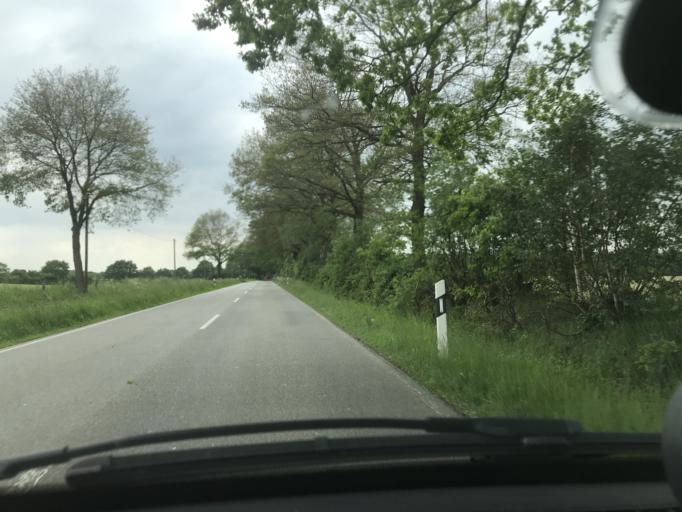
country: DE
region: Schleswig-Holstein
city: Siek
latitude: 53.6127
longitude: 10.3121
